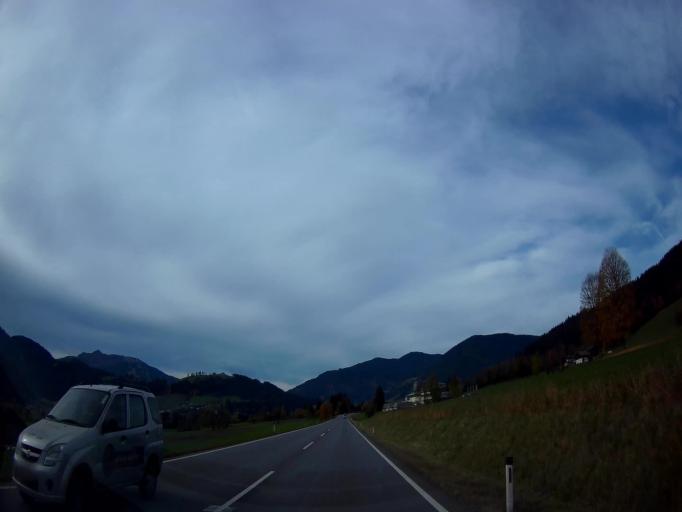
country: AT
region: Salzburg
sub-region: Politischer Bezirk Sankt Johann im Pongau
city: Radstadt
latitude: 47.3842
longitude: 13.4413
